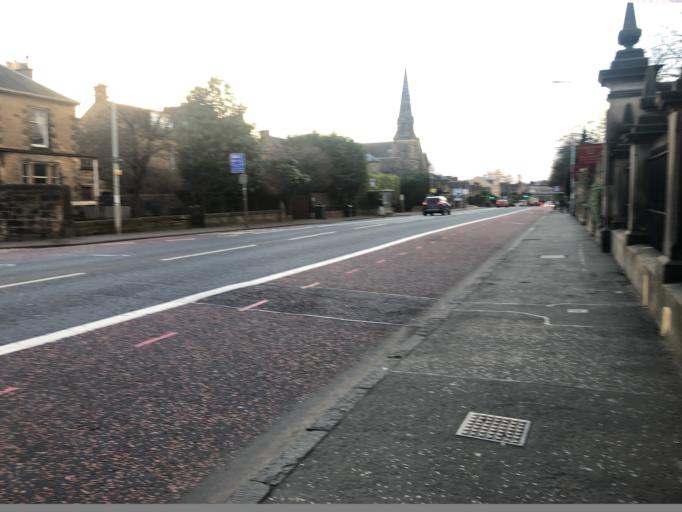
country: GB
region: Scotland
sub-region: Edinburgh
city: Edinburgh
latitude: 55.9459
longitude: -3.2274
